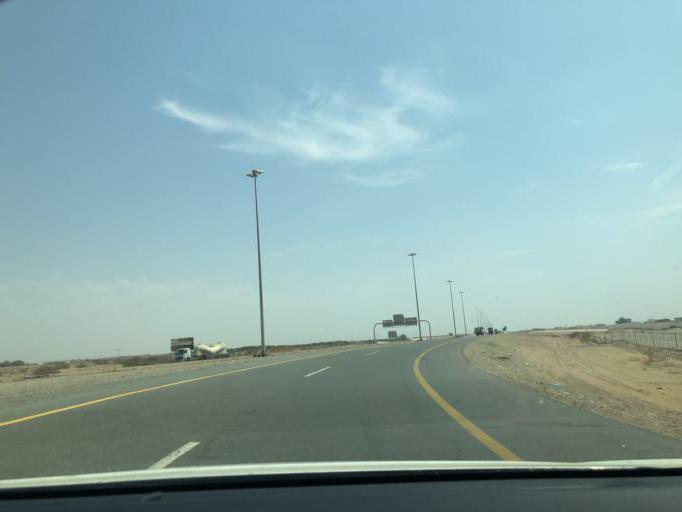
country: SA
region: Makkah
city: Rabigh
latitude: 22.2719
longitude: 39.1242
